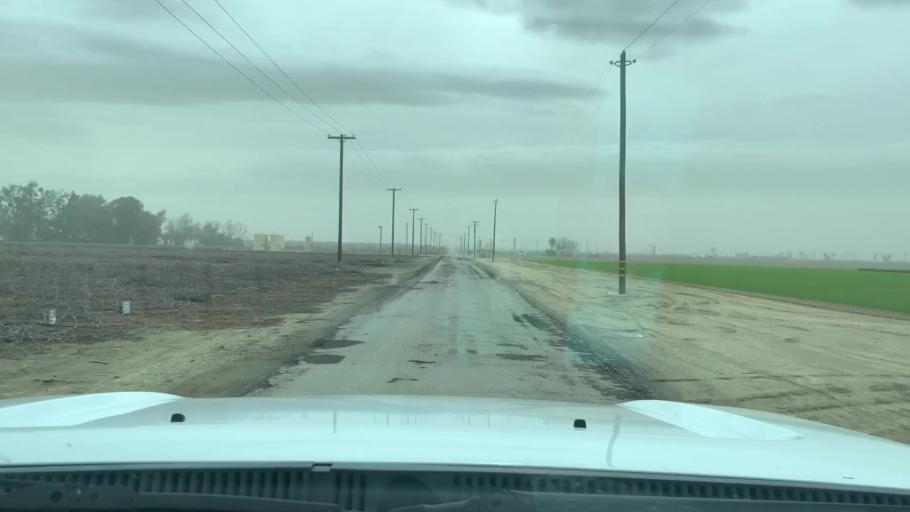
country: US
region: California
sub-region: Kern County
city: Shafter
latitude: 35.5347
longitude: -119.2689
